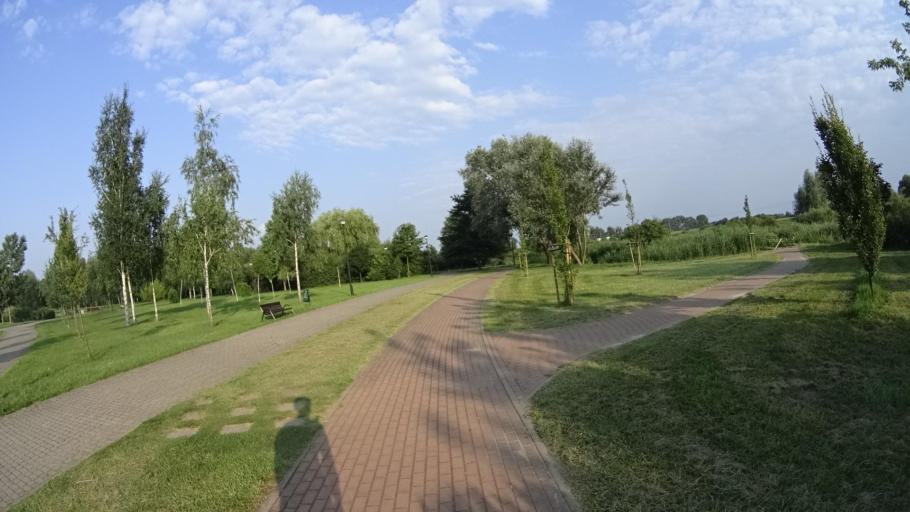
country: PL
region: Masovian Voivodeship
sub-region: Powiat pruszkowski
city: Raszyn
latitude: 52.1477
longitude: 20.9273
